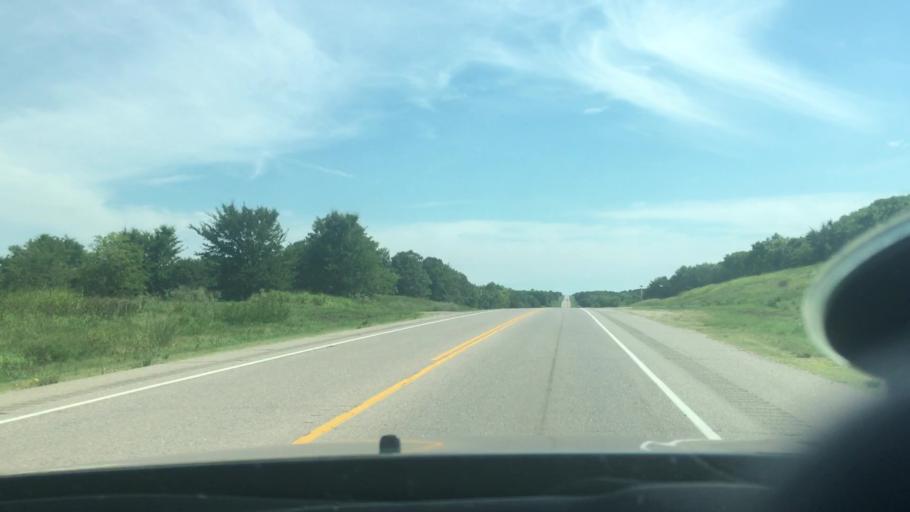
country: US
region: Oklahoma
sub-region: Seminole County
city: Maud
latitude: 35.1171
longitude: -96.6789
